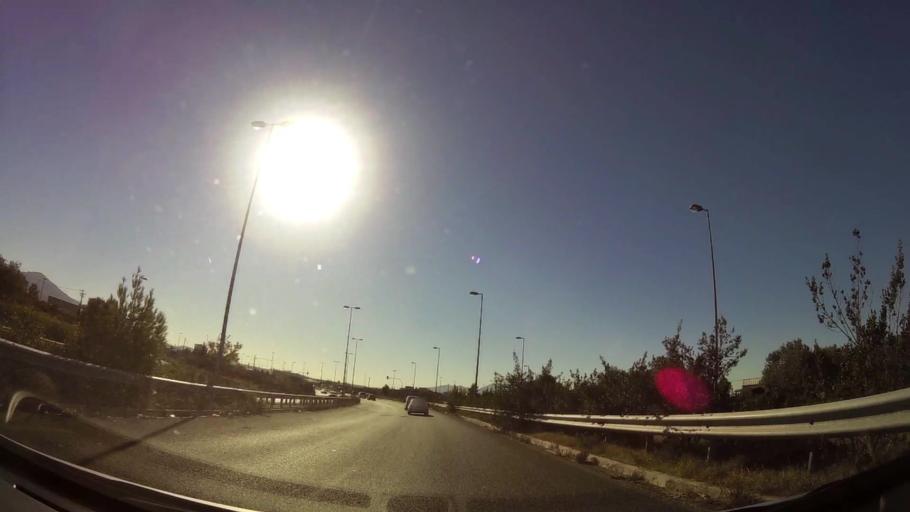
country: GR
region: Attica
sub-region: Nomarchia Anatolikis Attikis
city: Thrakomakedones
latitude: 38.1009
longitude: 23.7642
